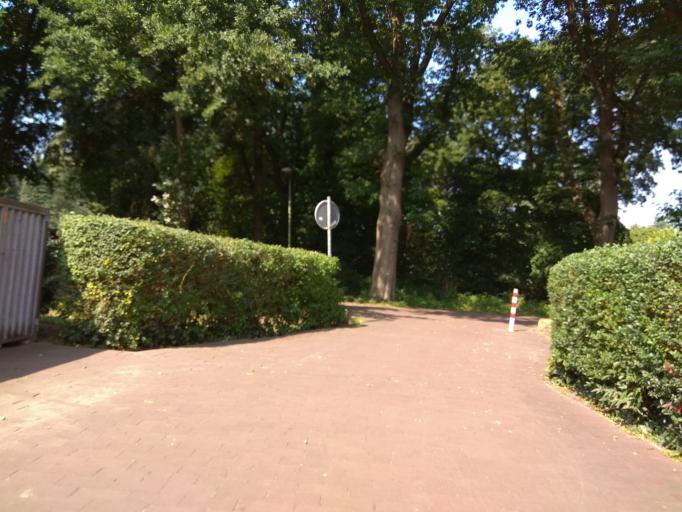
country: DE
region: North Rhine-Westphalia
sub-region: Regierungsbezirk Munster
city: Klein Reken
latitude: 51.7292
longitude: 7.0358
